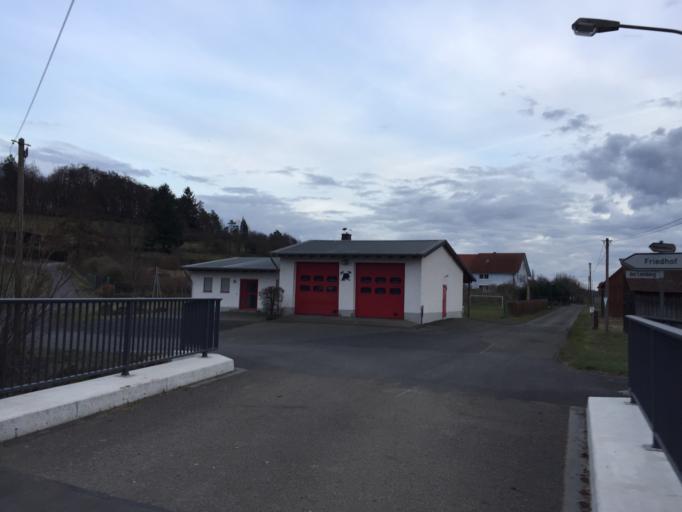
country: DE
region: Hesse
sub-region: Regierungsbezirk Giessen
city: Rabenau
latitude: 50.6602
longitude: 8.8925
